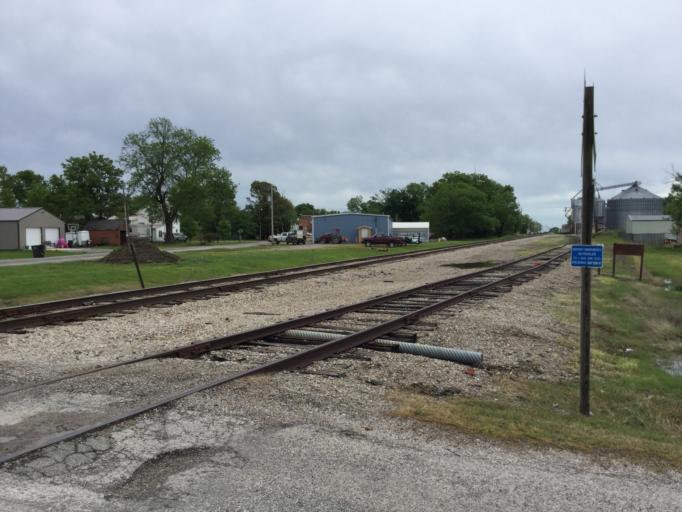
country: US
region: Kansas
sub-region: Labette County
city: Altamont
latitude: 37.1907
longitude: -95.3000
